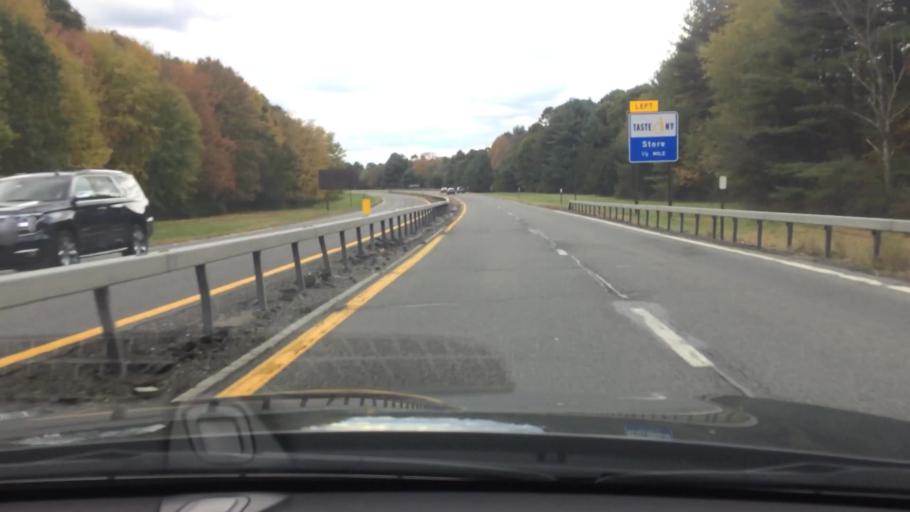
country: US
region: New York
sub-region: Dutchess County
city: Hillside Lake
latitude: 41.6654
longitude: -73.7900
